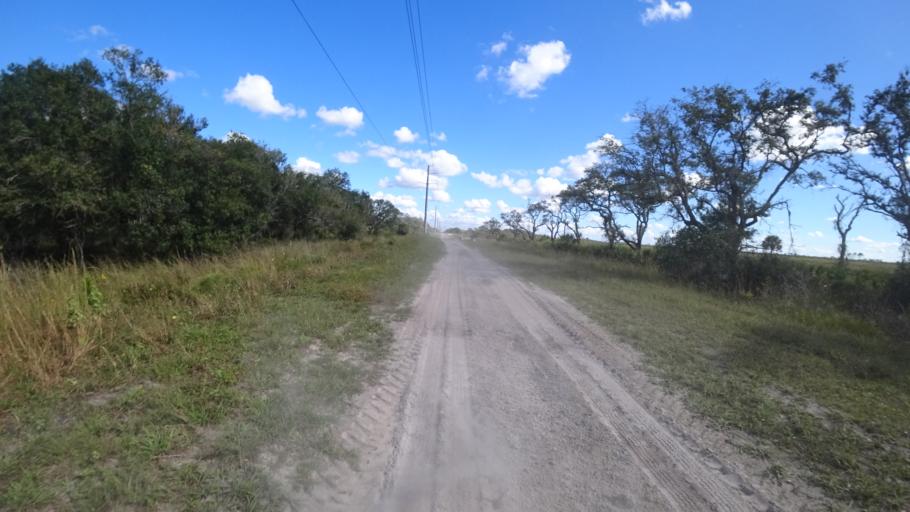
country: US
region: Florida
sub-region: Sarasota County
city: Lake Sarasota
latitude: 27.2450
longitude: -82.2731
